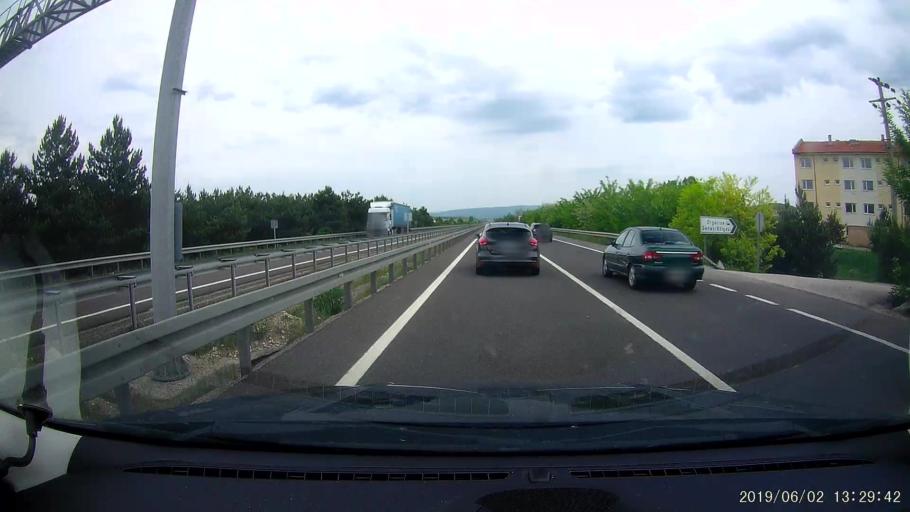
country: TR
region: Cankiri
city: Cerkes
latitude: 40.8118
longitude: 32.9313
